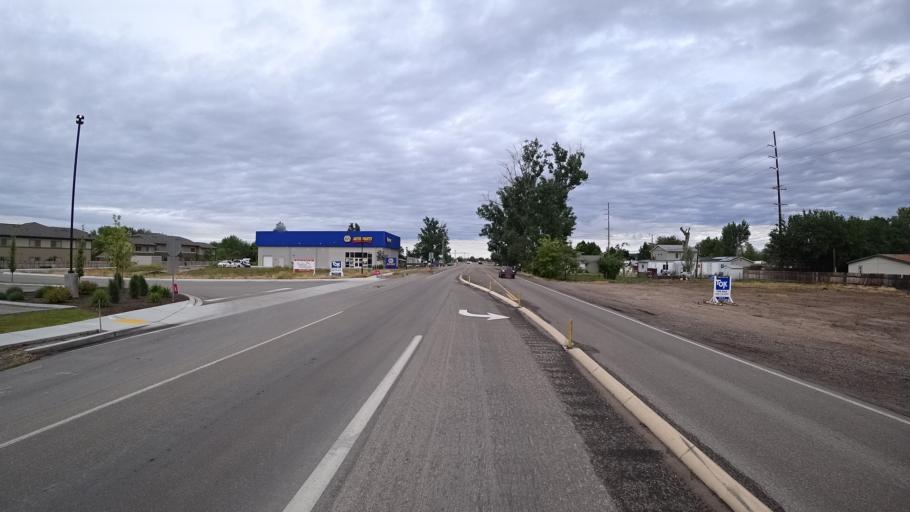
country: US
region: Idaho
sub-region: Ada County
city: Star
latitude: 43.6920
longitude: -116.4958
